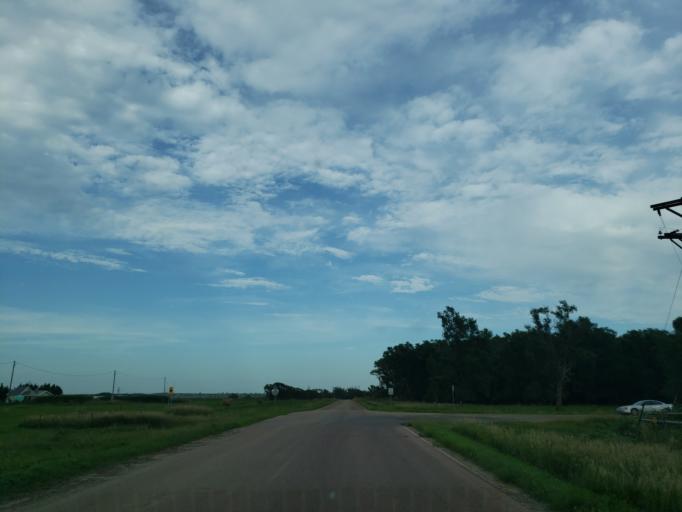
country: US
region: South Dakota
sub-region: Davison County
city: Mitchell
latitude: 43.6879
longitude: -97.9871
